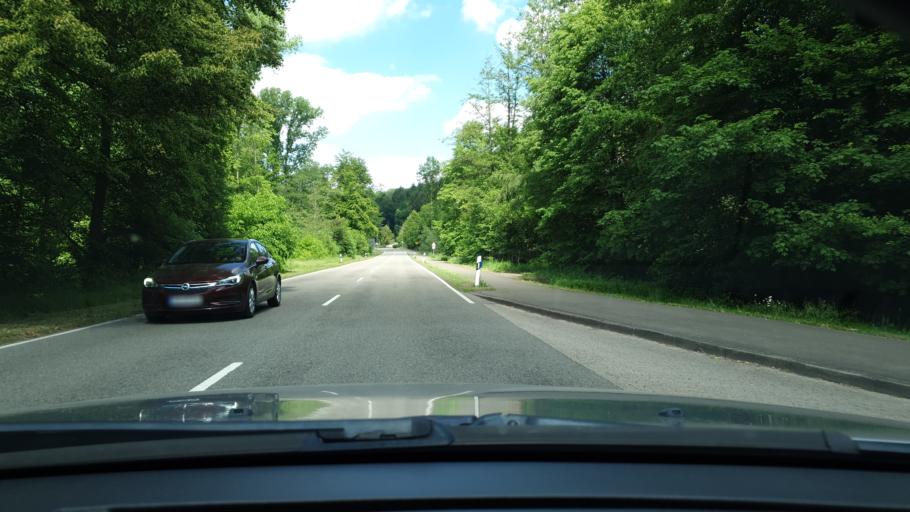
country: DE
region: Saarland
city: Homburg
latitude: 49.3323
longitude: 7.3649
